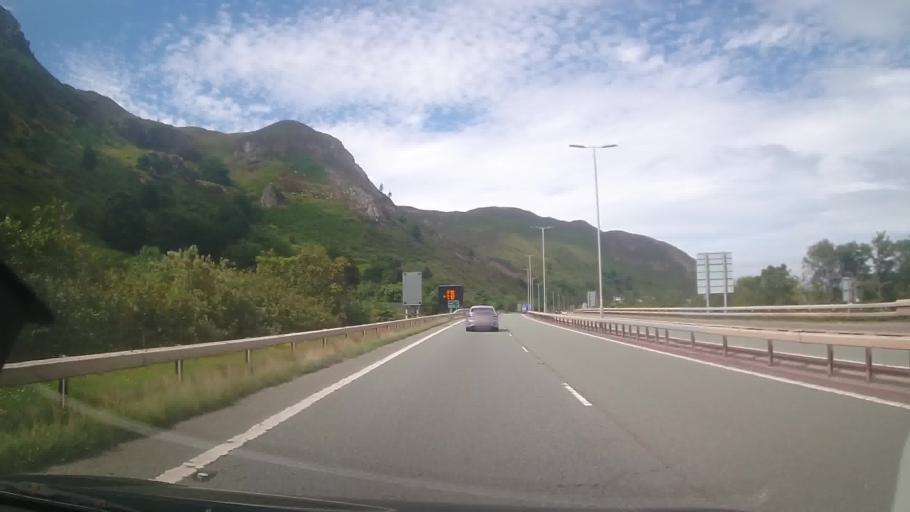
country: GB
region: Wales
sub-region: Conwy
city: Conwy
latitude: 53.2871
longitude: -3.8603
